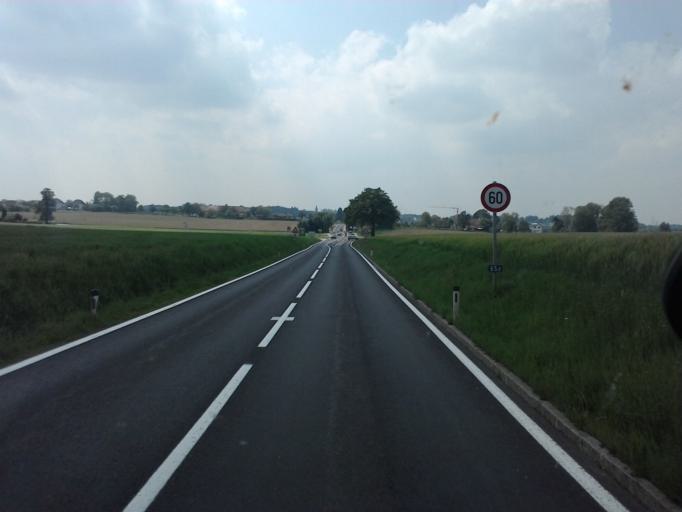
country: AT
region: Upper Austria
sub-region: Wels-Land
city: Sattledt
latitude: 48.0720
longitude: 14.0720
